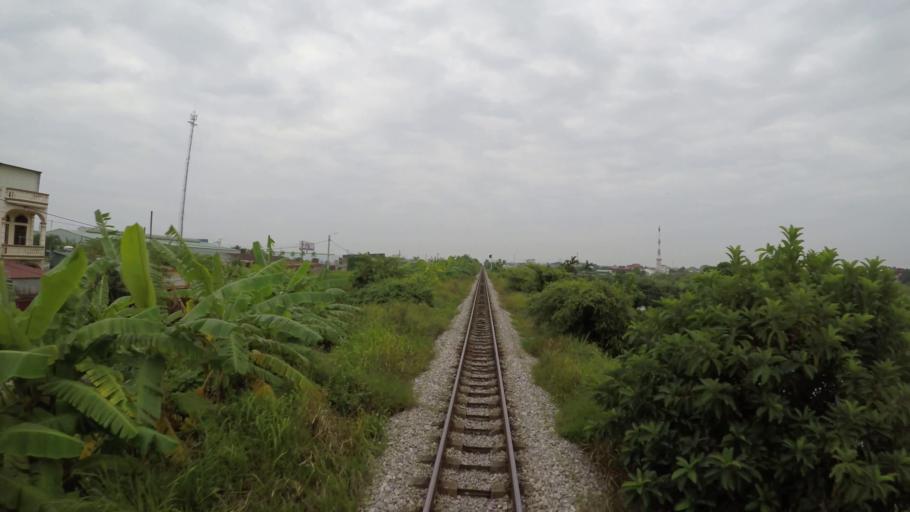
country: VN
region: Hai Duong
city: Thanh Pho Hai Duong
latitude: 20.9443
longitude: 106.3602
